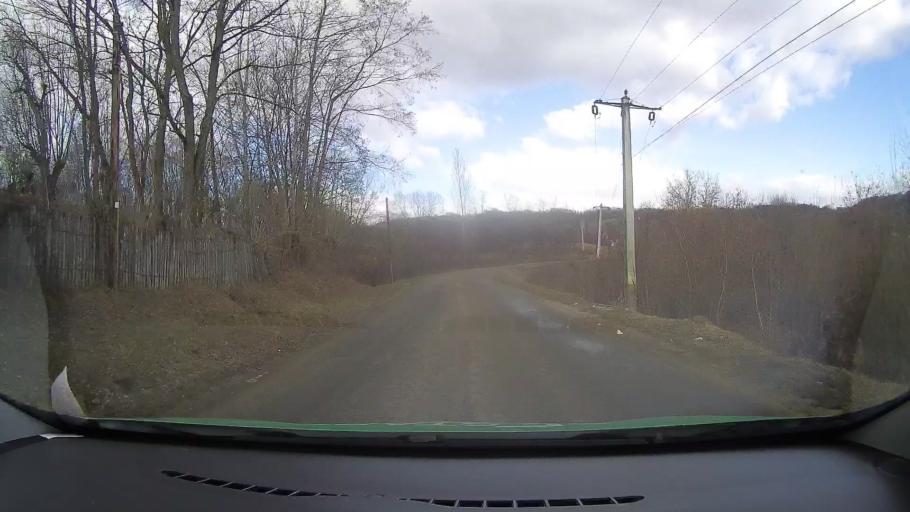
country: RO
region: Dambovita
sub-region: Comuna Buciumeni
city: Buciumeni
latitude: 45.1335
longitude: 25.4675
